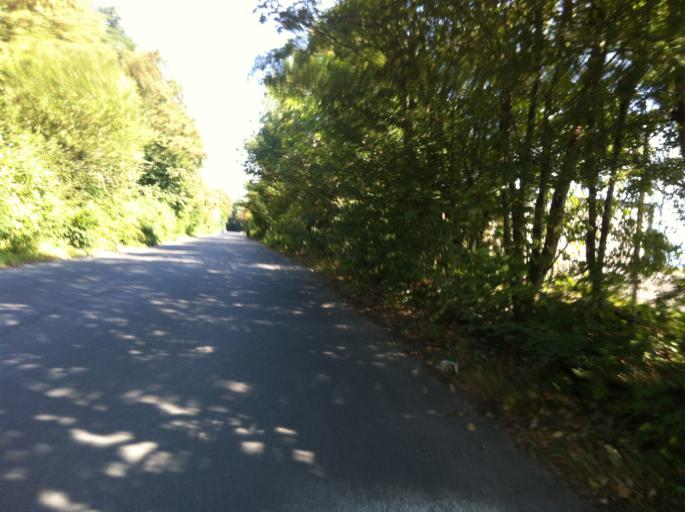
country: DE
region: North Rhine-Westphalia
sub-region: Regierungsbezirk Koln
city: Hoehenberg
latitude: 50.9138
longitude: 7.0219
